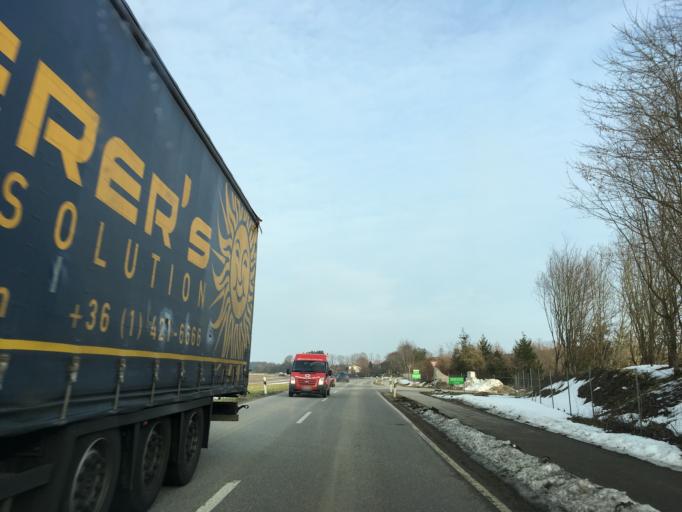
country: DE
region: Bavaria
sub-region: Upper Bavaria
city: Sochtenau
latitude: 47.9361
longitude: 12.2386
